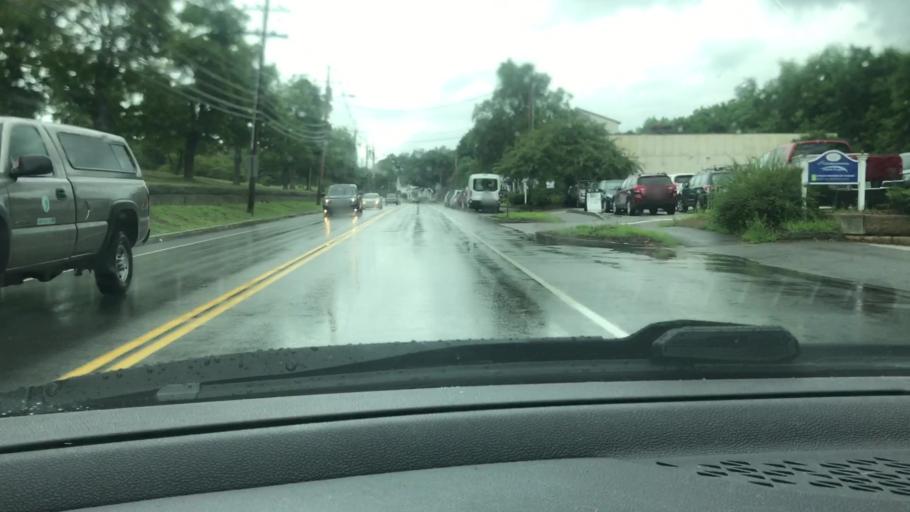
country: US
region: New Hampshire
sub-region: Merrimack County
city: Concord
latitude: 43.2207
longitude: -71.5509
